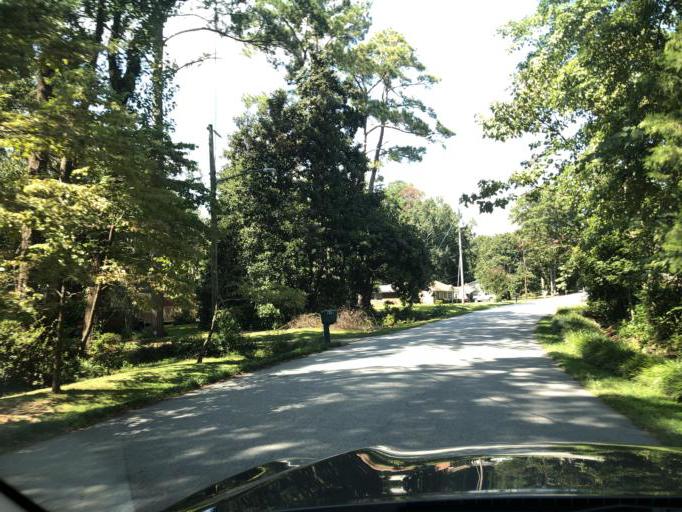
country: US
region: Georgia
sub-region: Muscogee County
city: Columbus
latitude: 32.5374
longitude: -84.9272
